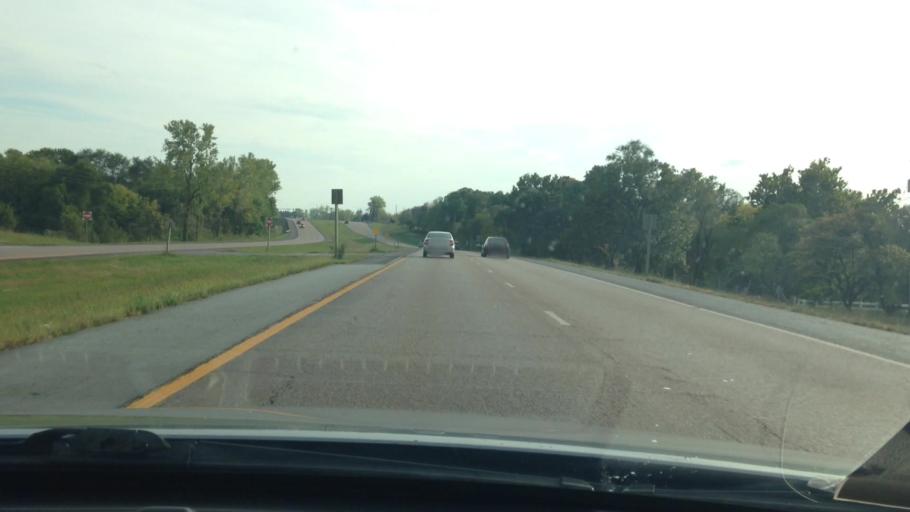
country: US
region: Kansas
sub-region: Leavenworth County
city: Basehor
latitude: 39.1350
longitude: -94.9008
